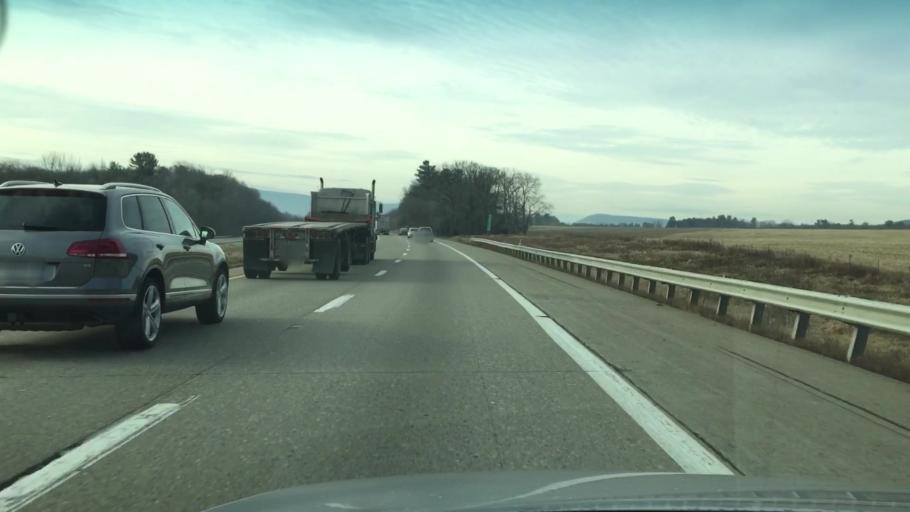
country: US
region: Pennsylvania
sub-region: Luzerne County
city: Conyngham
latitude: 41.0143
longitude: -76.1262
